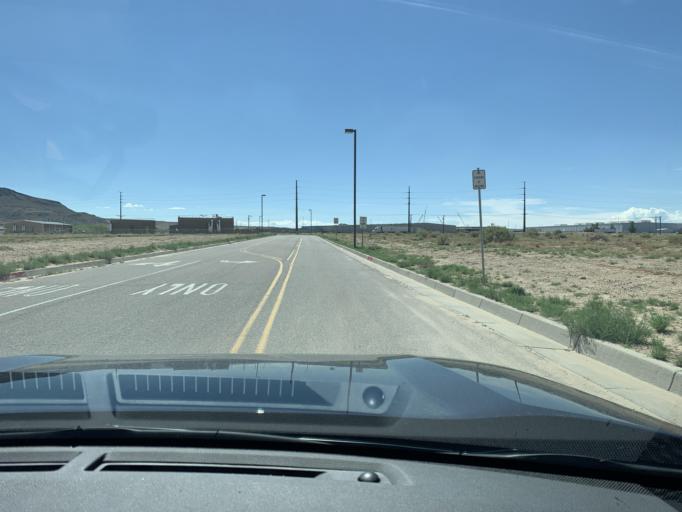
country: US
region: New Mexico
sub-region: Valencia County
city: Los Lunas
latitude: 34.8218
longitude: -106.7625
